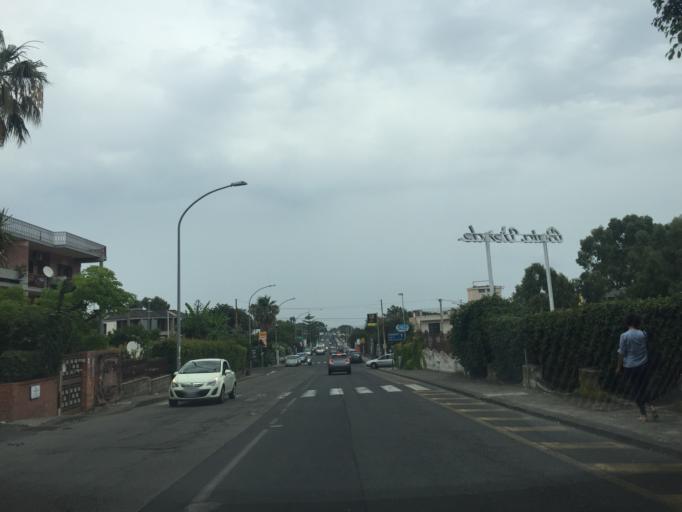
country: IT
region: Sicily
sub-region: Catania
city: Aci Castello
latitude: 37.5406
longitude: 15.1326
